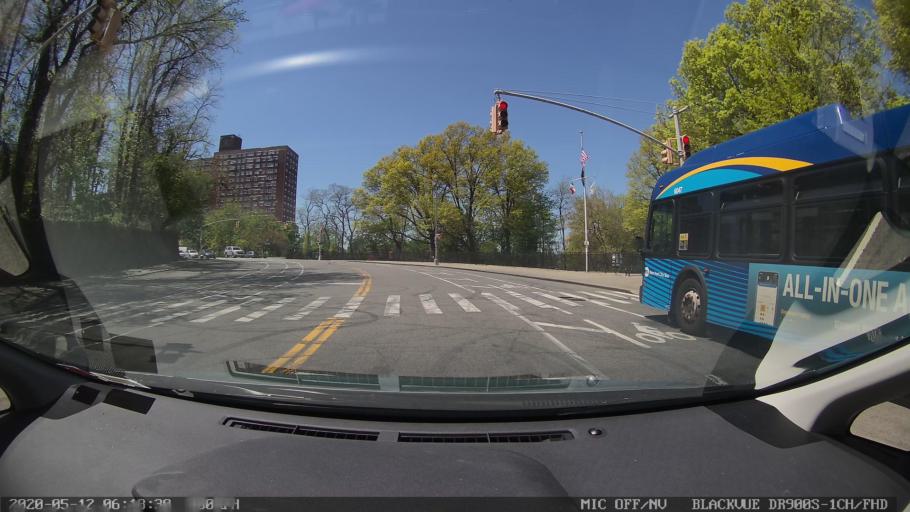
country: US
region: New York
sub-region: New York County
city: Inwood
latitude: 40.8582
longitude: -73.9253
